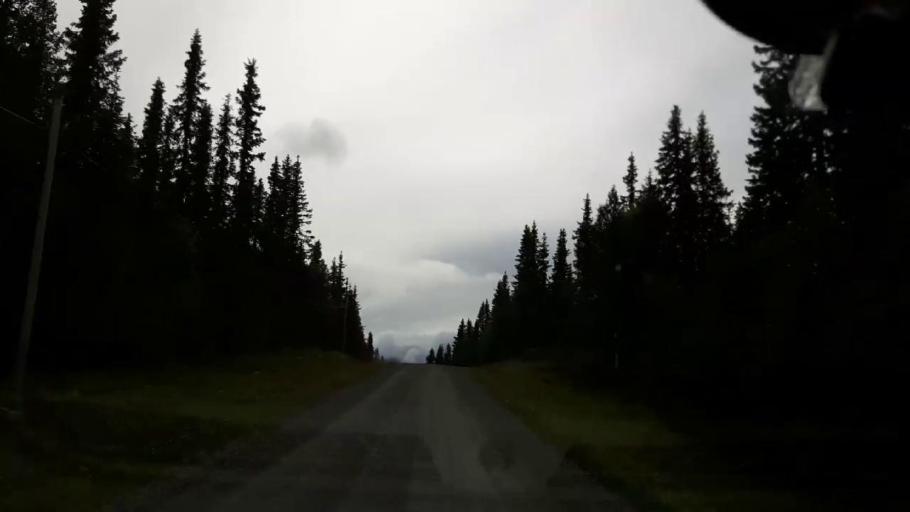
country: SE
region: Jaemtland
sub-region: Krokoms Kommun
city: Valla
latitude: 63.7731
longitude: 13.8296
